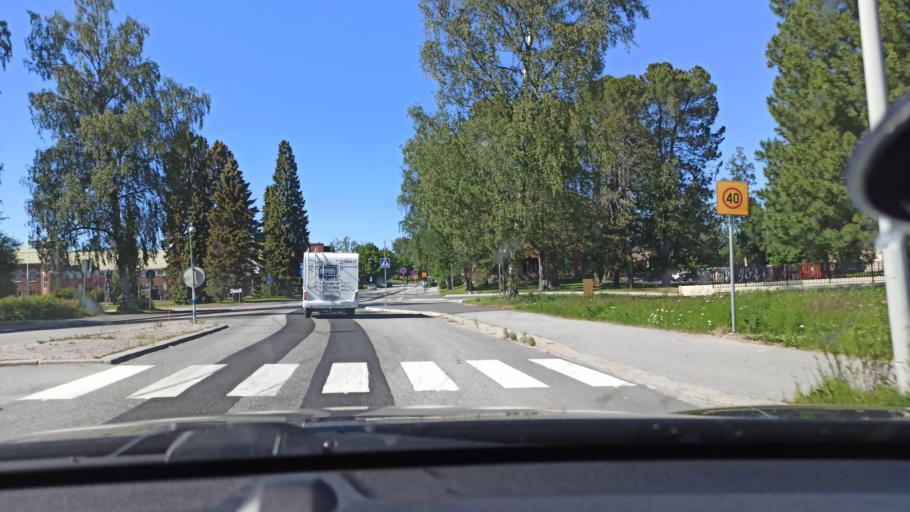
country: FI
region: Ostrobothnia
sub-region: Jakobstadsregionen
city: Jakobstad
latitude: 63.6743
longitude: 22.7129
